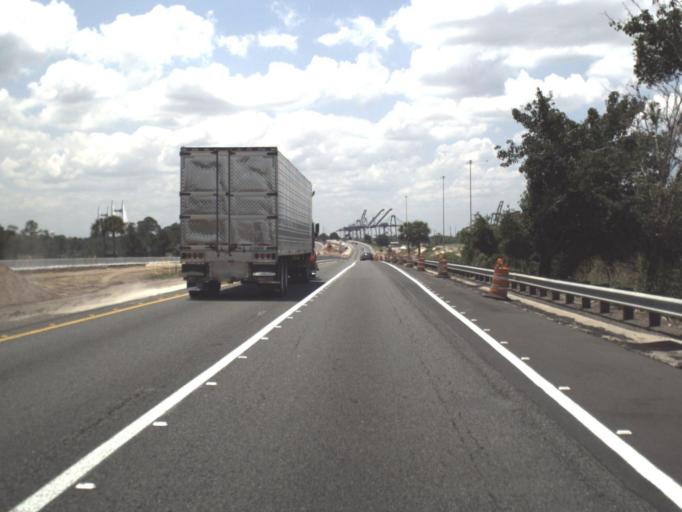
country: US
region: Florida
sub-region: Duval County
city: Jacksonville
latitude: 30.4117
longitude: -81.5649
